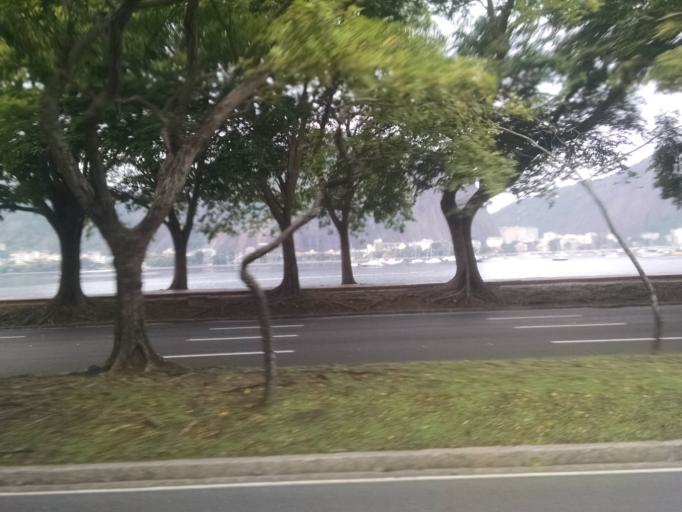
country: BR
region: Rio de Janeiro
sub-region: Rio De Janeiro
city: Rio de Janeiro
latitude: -22.9427
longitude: -43.1727
